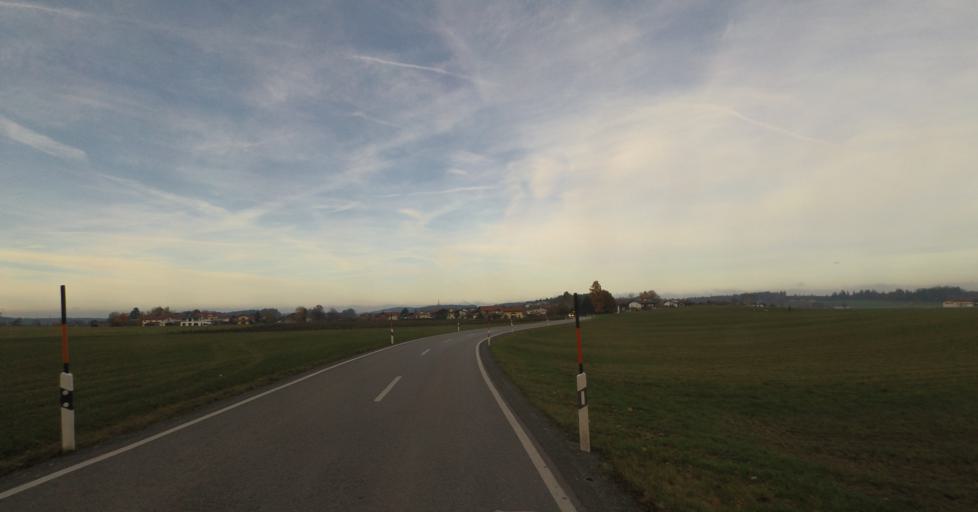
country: DE
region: Bavaria
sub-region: Upper Bavaria
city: Vachendorf
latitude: 47.8755
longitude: 12.6084
